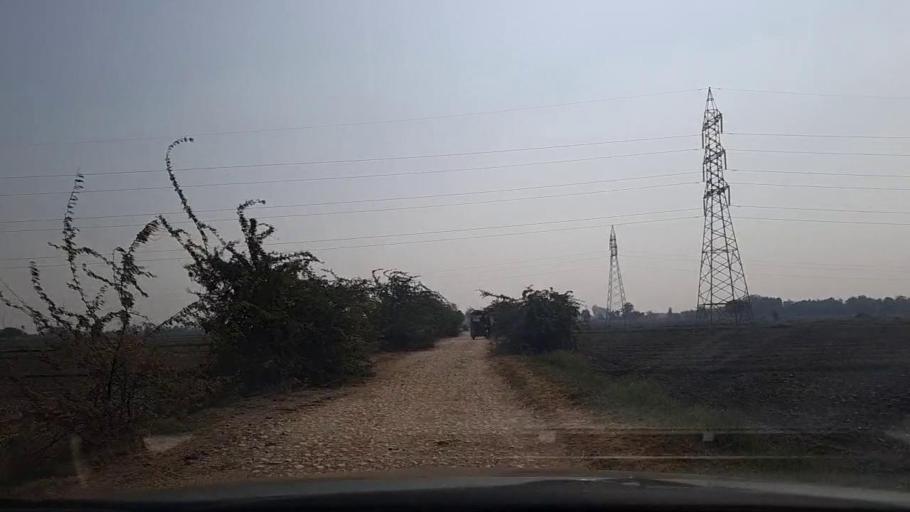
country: PK
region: Sindh
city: Mirpur Sakro
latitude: 24.5686
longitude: 67.7763
